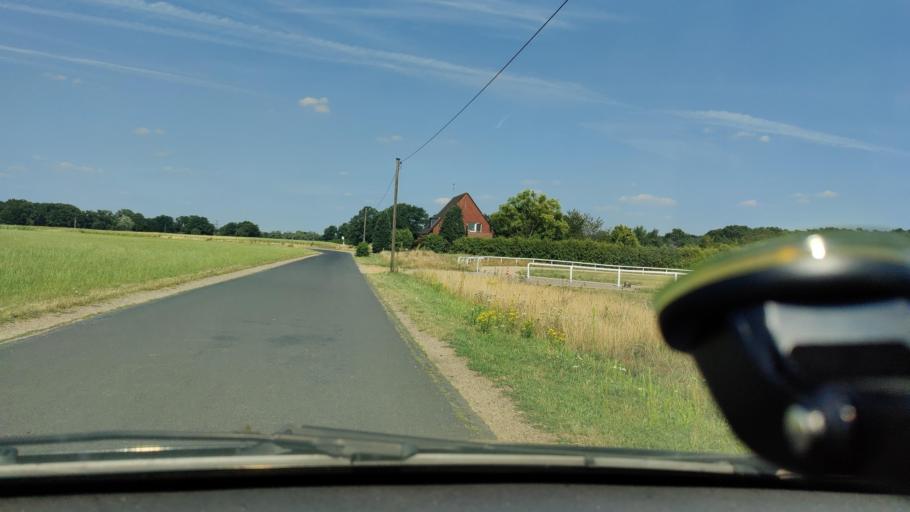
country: DE
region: North Rhine-Westphalia
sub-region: Regierungsbezirk Dusseldorf
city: Schermbeck
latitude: 51.6475
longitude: 6.9013
